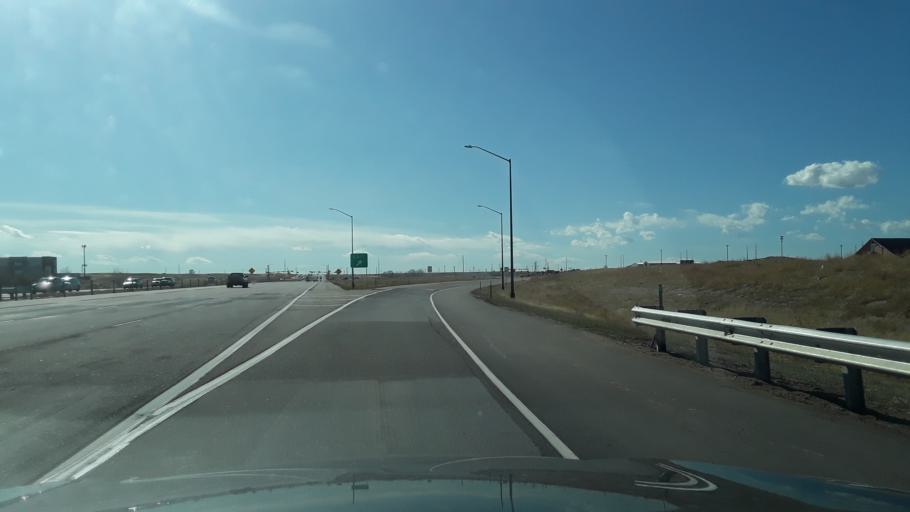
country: US
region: Colorado
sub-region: Pueblo County
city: Pueblo
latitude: 38.3133
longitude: -104.6543
